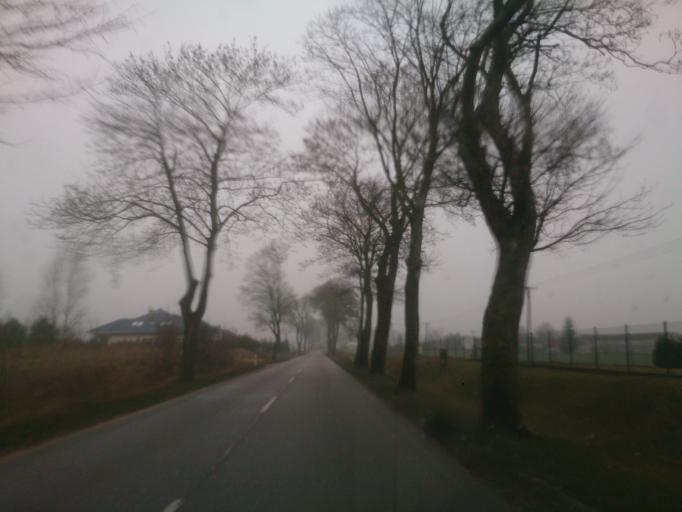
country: PL
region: Pomeranian Voivodeship
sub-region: Powiat starogardzki
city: Lubichowo
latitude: 53.8612
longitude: 18.3879
